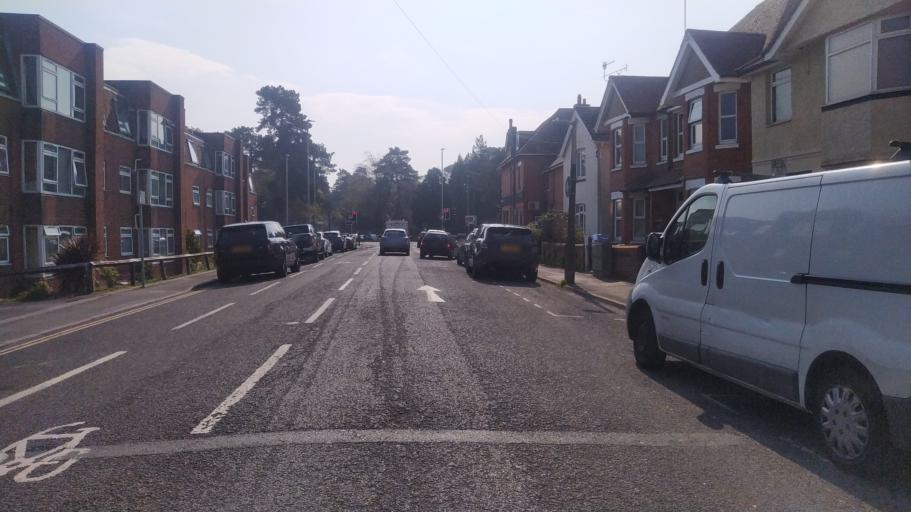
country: GB
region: England
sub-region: Dorset
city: Parkstone
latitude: 50.7240
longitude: -1.9263
